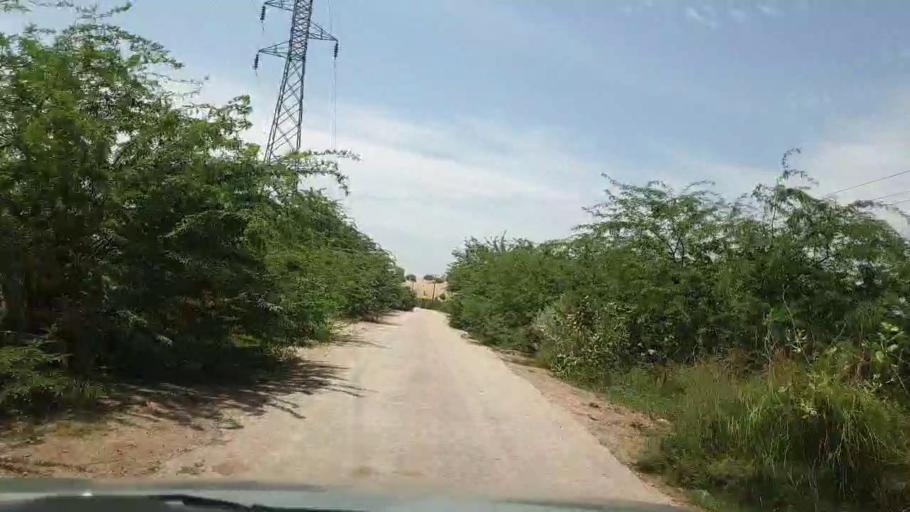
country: PK
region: Sindh
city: Bozdar
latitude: 27.0803
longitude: 68.9661
